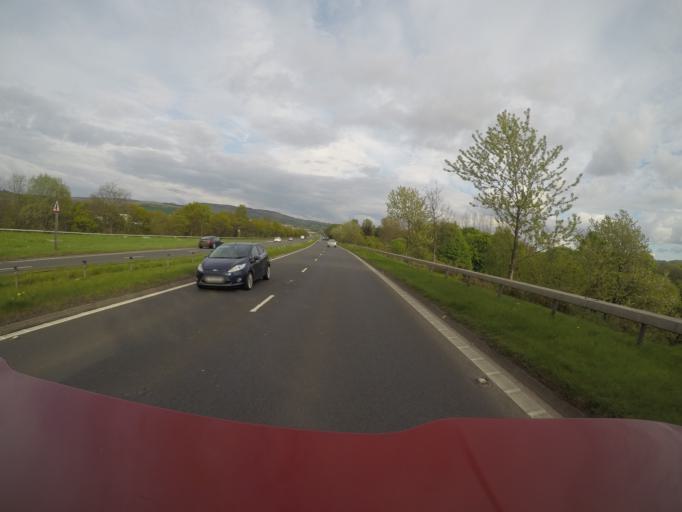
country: GB
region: Scotland
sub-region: West Dunbartonshire
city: Renton
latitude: 55.9612
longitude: -4.5824
